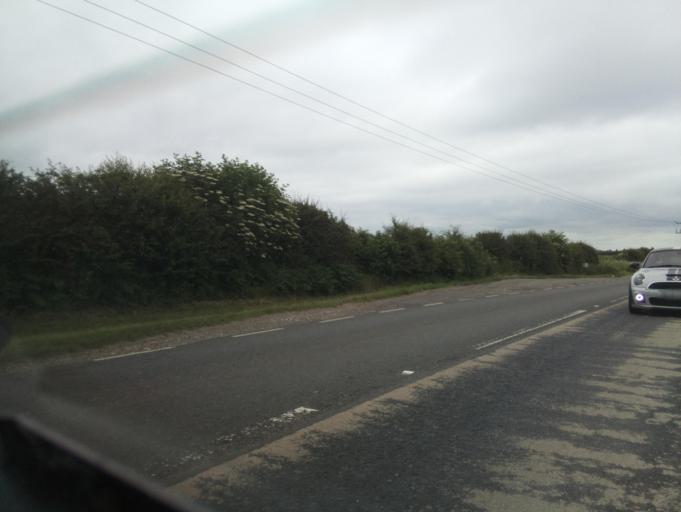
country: GB
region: England
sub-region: Nottinghamshire
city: East Leake
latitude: 52.8151
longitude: -1.1667
